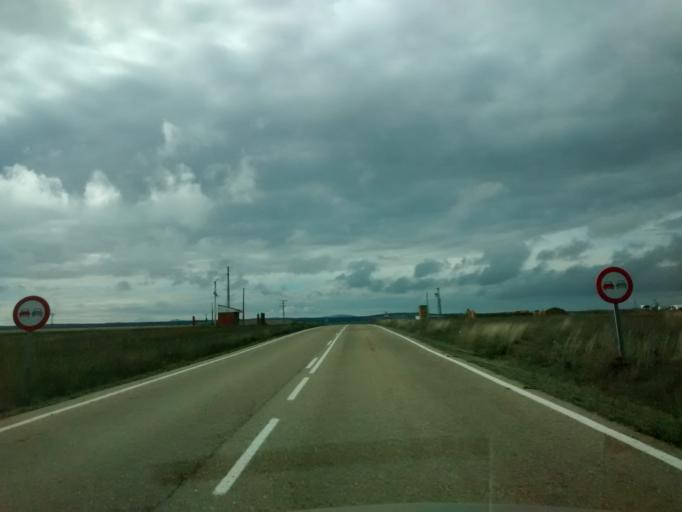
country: ES
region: Aragon
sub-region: Provincia de Zaragoza
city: Used
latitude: 40.9932
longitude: -1.5763
